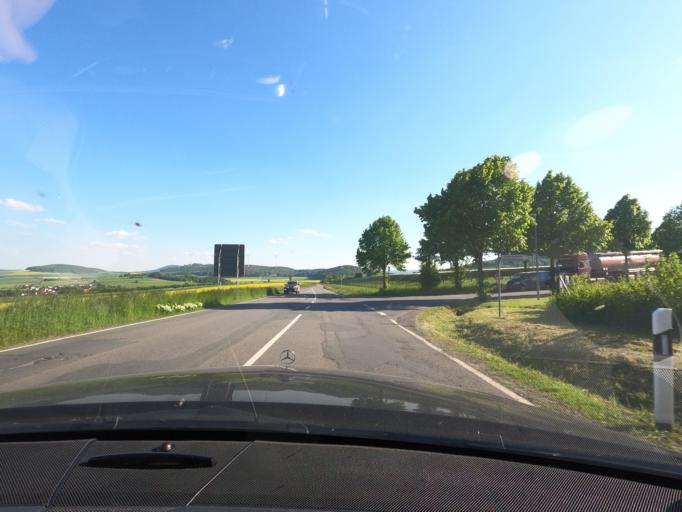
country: DE
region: Hesse
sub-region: Regierungsbezirk Kassel
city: Breuna
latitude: 51.3986
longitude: 9.1841
